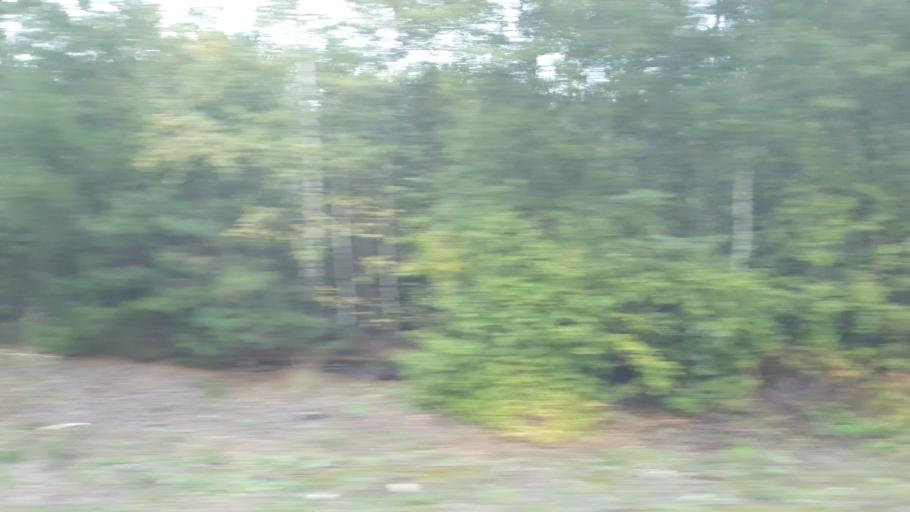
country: DE
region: Saarland
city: Sankt Ingbert
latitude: 49.2750
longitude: 7.1665
